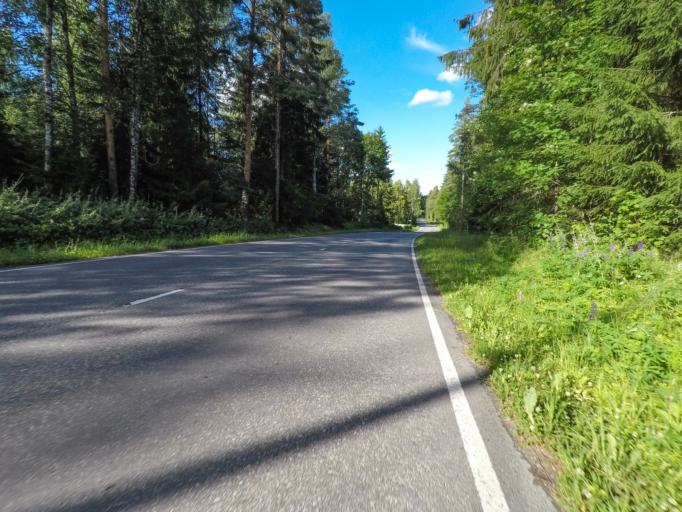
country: FI
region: South Karelia
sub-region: Imatra
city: Imatra
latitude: 61.1437
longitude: 28.7454
